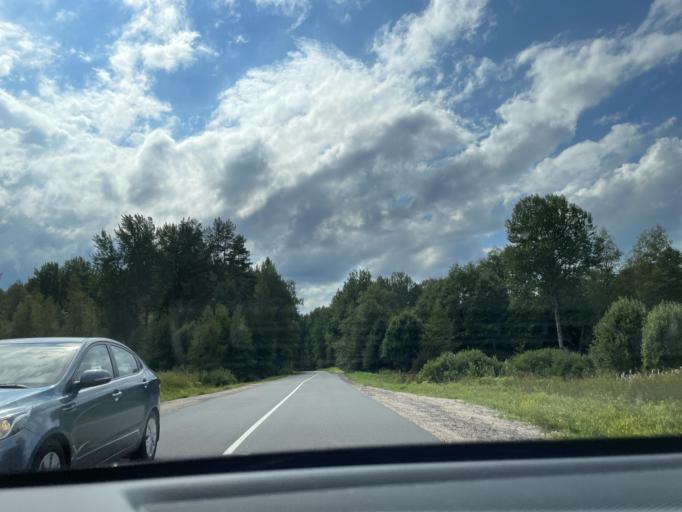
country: RU
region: Novgorod
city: Valday
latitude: 58.0127
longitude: 33.1792
